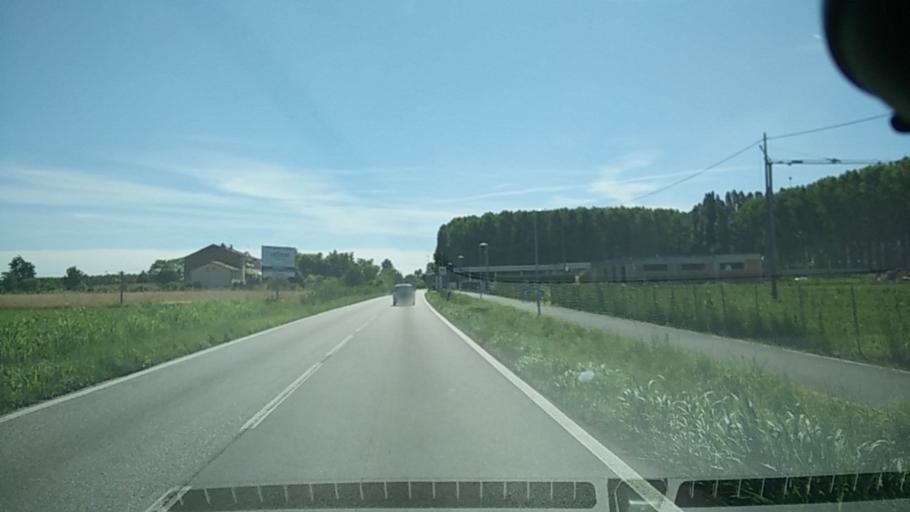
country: IT
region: Veneto
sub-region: Provincia di Venezia
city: Moniego
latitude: 45.5779
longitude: 12.0823
